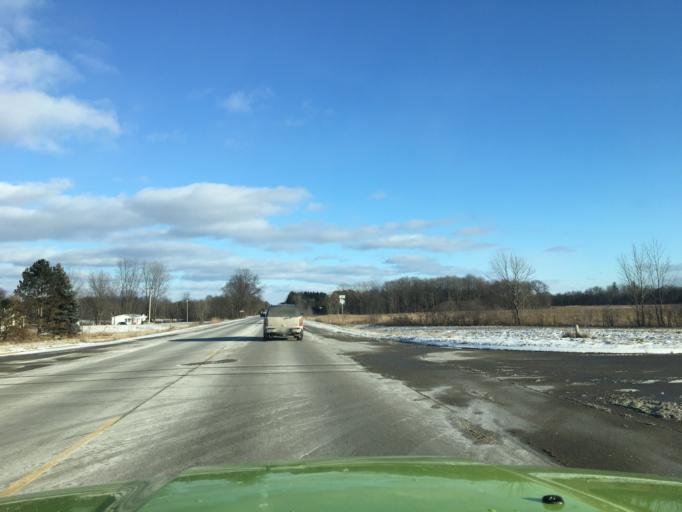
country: US
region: Michigan
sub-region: Kent County
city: Cedar Springs
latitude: 43.1757
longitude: -85.5010
